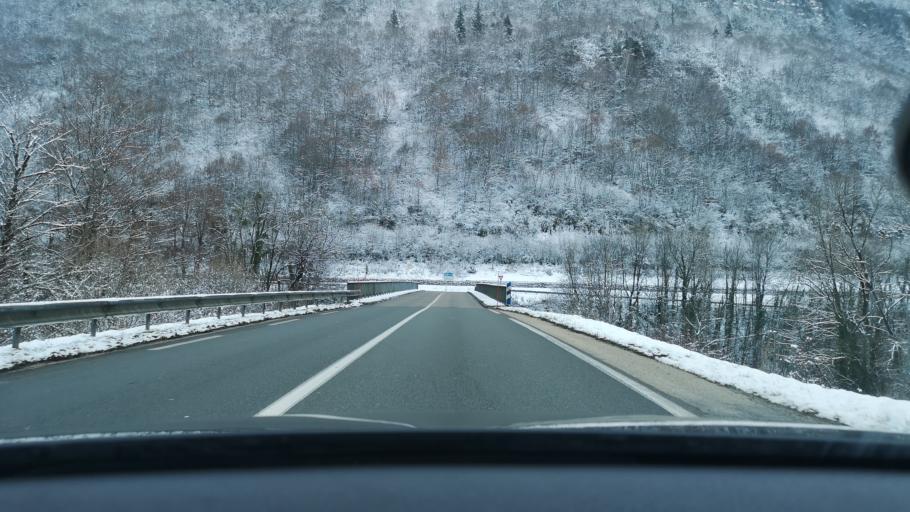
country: FR
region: Rhone-Alpes
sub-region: Departement de l'Ain
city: Dortan
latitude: 46.3633
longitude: 5.7062
